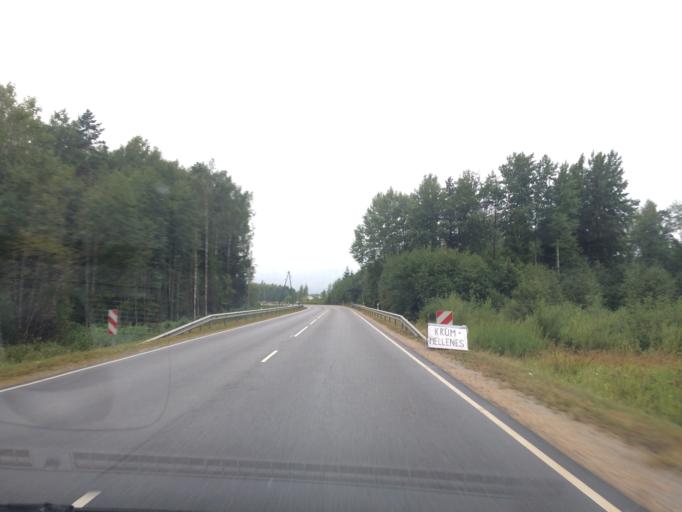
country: LV
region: Ogre
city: Ogre
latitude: 56.8593
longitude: 24.6304
